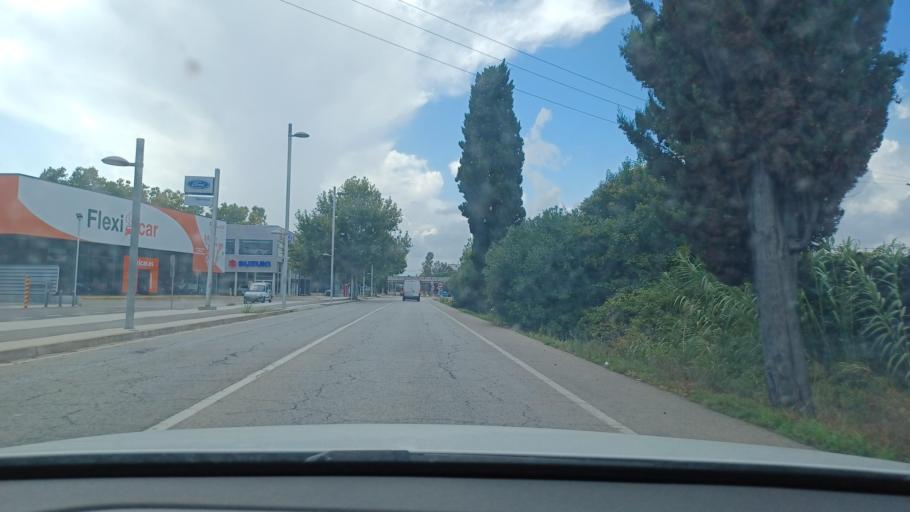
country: ES
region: Catalonia
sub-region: Provincia de Tarragona
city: Tarragona
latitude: 41.1166
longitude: 1.2305
